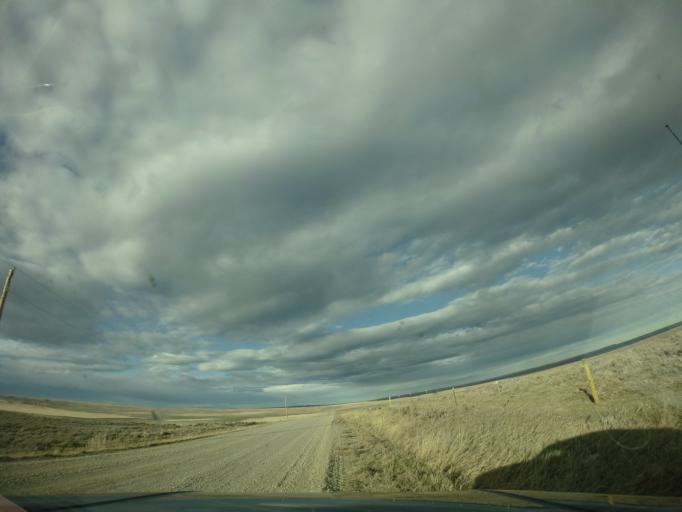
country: US
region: Montana
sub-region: Yellowstone County
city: Laurel
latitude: 45.9271
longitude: -108.8805
